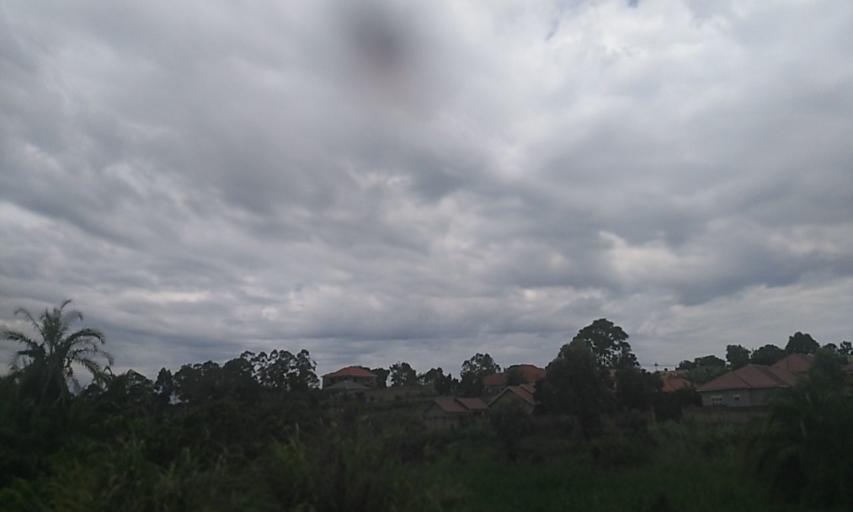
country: UG
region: Central Region
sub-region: Wakiso District
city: Bweyogerere
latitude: 0.3977
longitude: 32.6729
